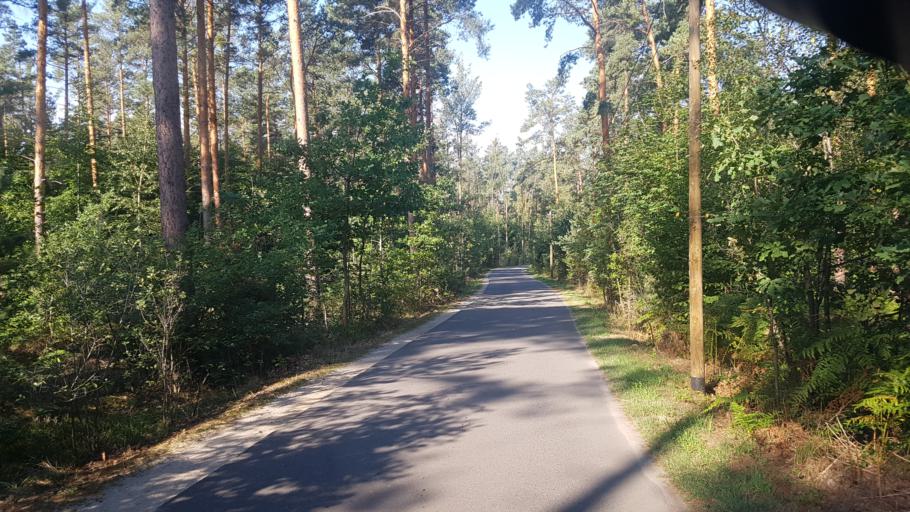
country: DE
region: Brandenburg
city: Plessa
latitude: 51.5269
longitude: 13.6601
